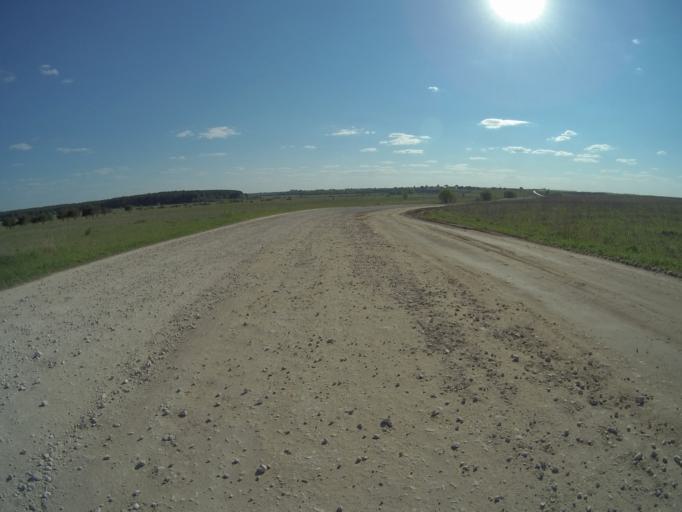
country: RU
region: Vladimir
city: Kideksha
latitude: 56.3741
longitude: 40.5546
